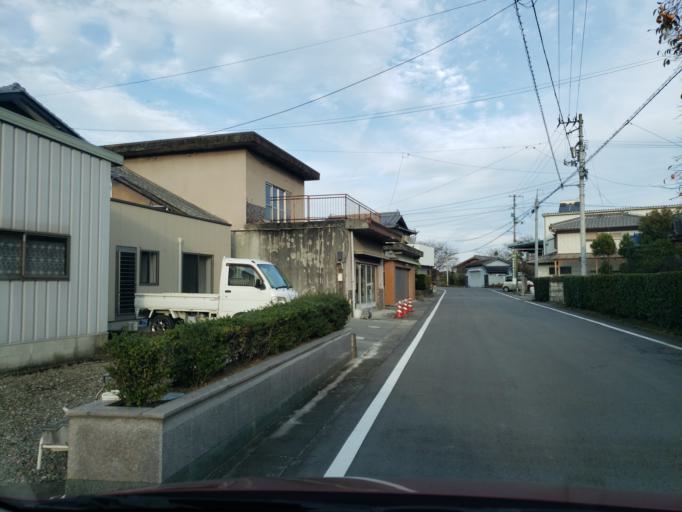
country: JP
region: Tokushima
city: Wakimachi
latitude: 34.0742
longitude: 134.2370
